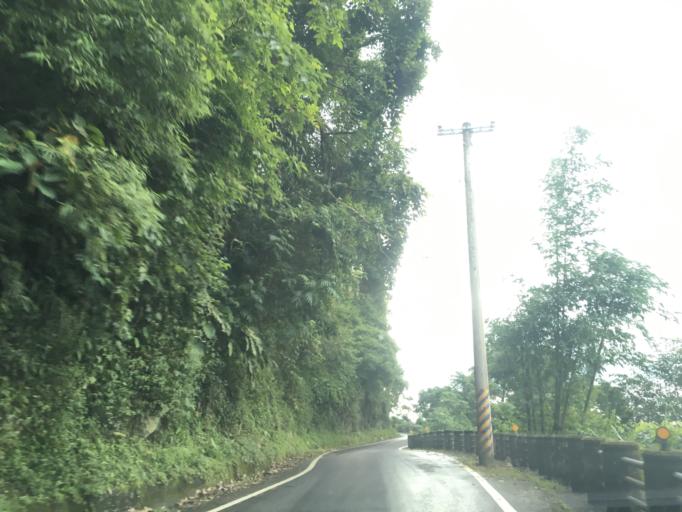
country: TW
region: Taiwan
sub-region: Chiayi
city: Jiayi Shi
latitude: 23.4441
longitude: 120.6603
